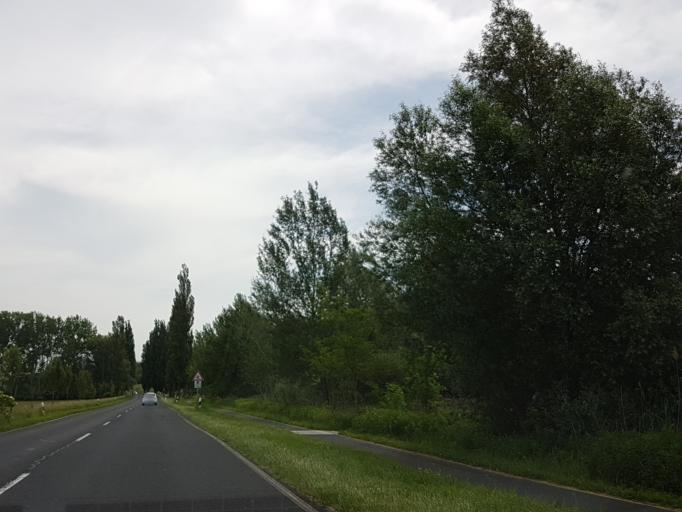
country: HU
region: Veszprem
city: Tapolca
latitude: 46.8063
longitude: 17.4253
